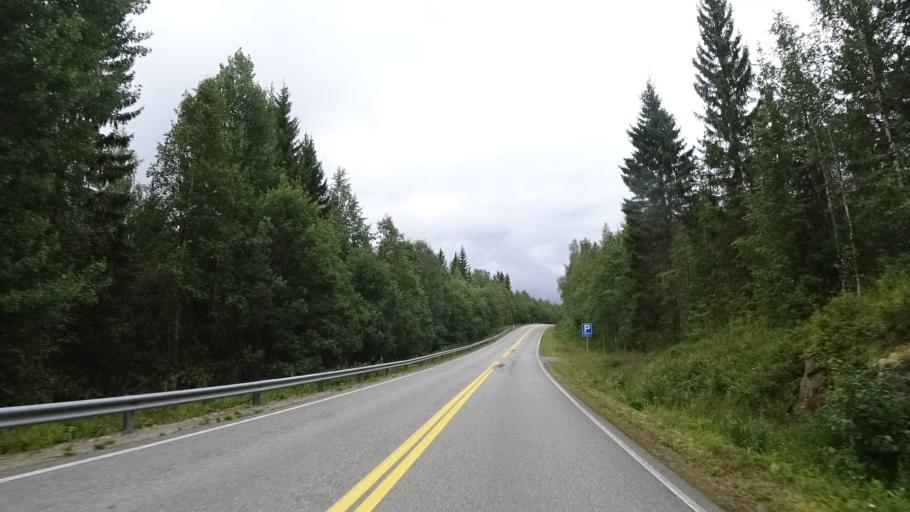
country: FI
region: North Karelia
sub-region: Joensuu
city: Ilomantsi
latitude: 63.2613
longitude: 30.6855
